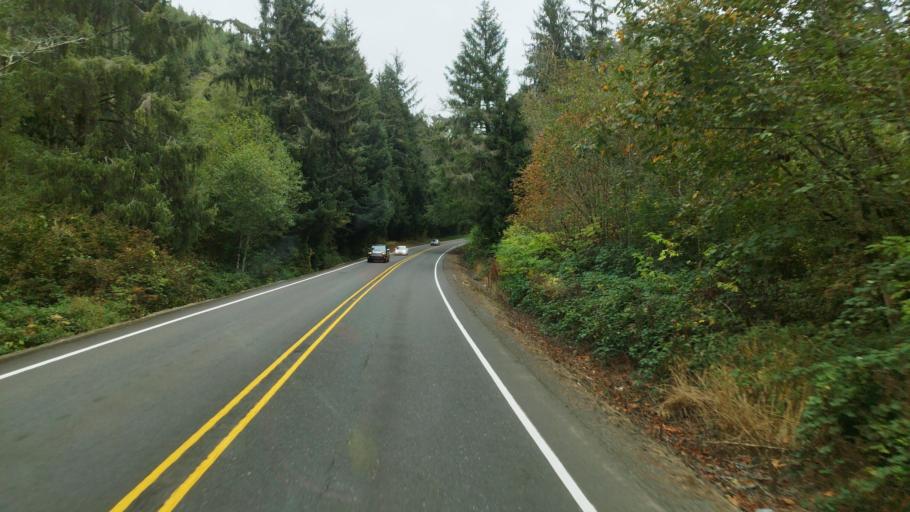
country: US
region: Oregon
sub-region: Clatsop County
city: Cannon Beach
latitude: 45.9026
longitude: -123.8586
